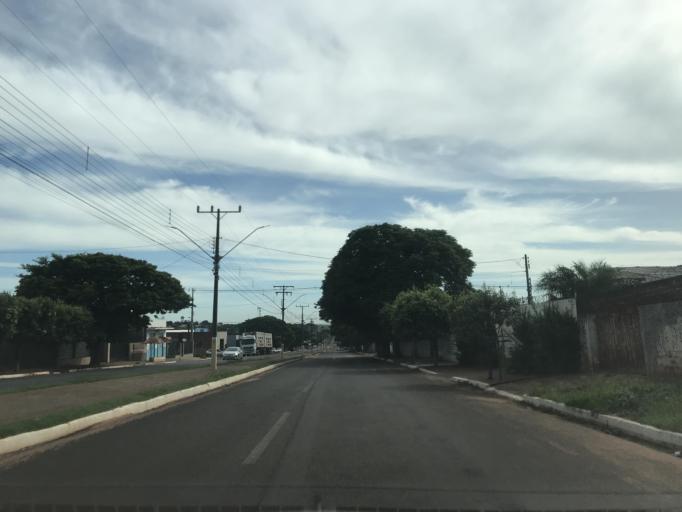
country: BR
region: Parana
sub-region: Paranavai
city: Nova Aurora
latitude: -22.9434
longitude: -52.6920
